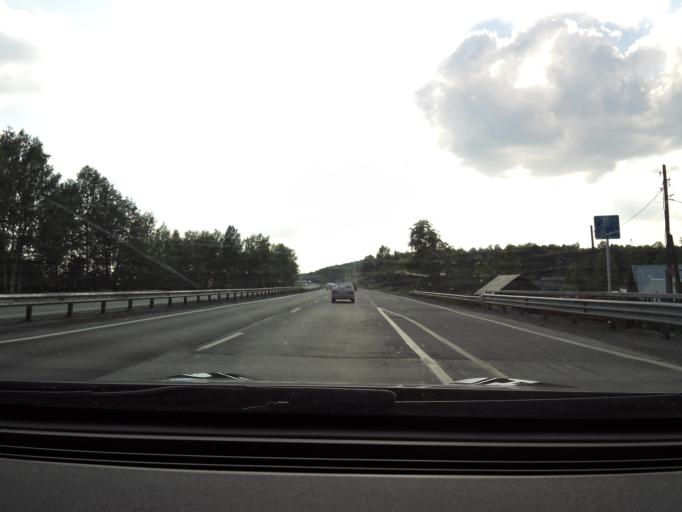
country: RU
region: Sverdlovsk
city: Severka
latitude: 56.8447
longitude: 60.2181
